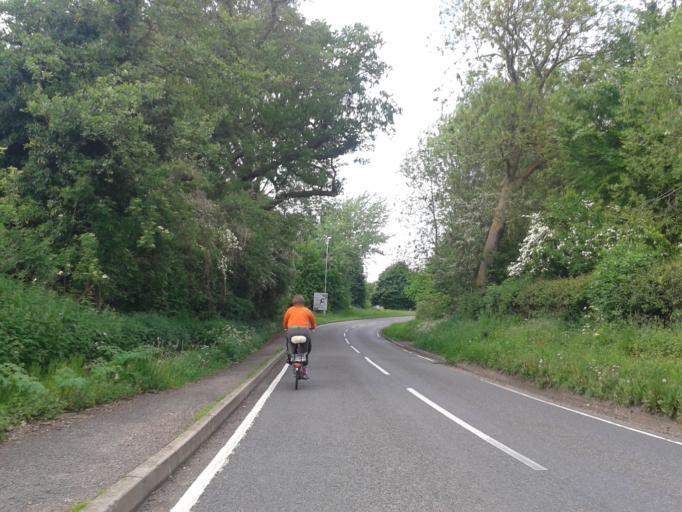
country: GB
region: England
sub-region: Northamptonshire
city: Oundle
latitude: 52.4867
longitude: -0.4582
